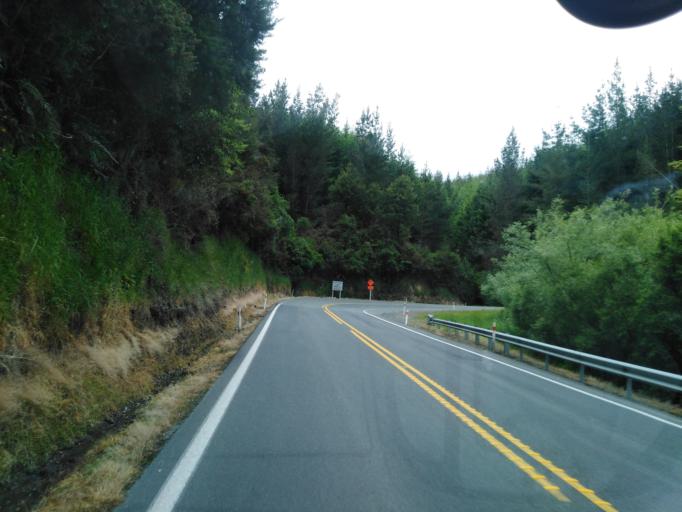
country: NZ
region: Tasman
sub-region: Tasman District
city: Wakefield
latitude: -41.6260
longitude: 172.7282
